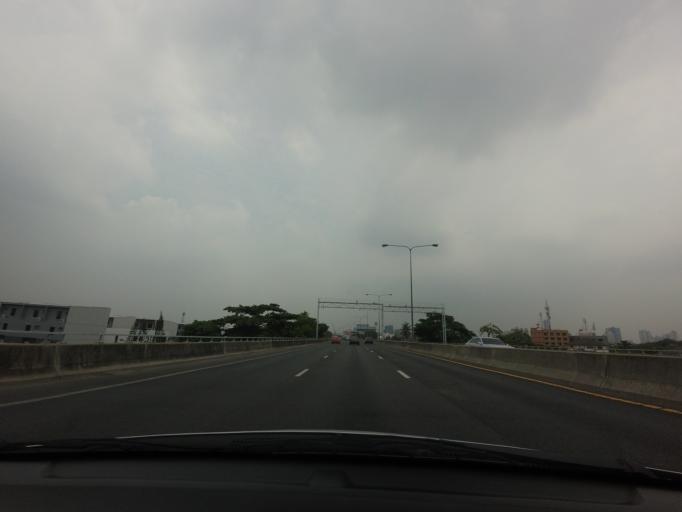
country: TH
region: Bangkok
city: Watthana
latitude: 13.7316
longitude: 100.6043
